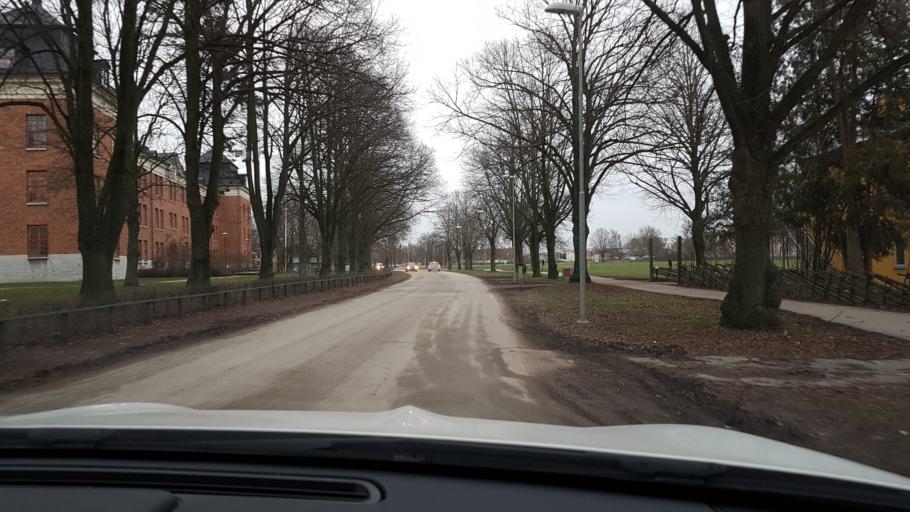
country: SE
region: Gotland
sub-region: Gotland
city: Visby
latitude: 57.6328
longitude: 18.2993
